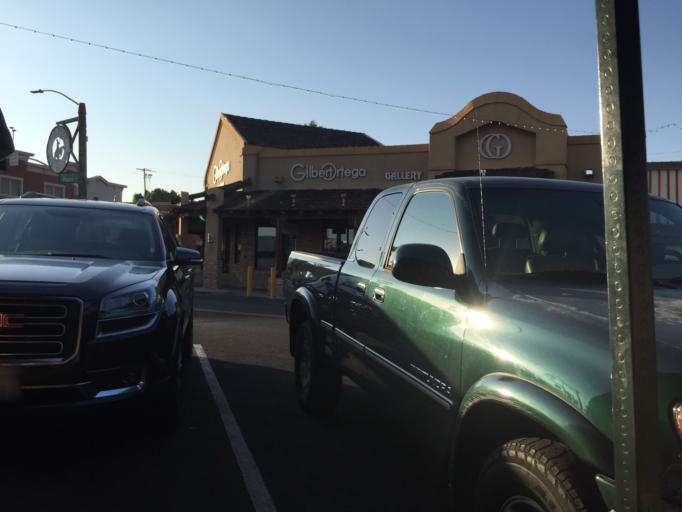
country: US
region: Arizona
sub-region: Maricopa County
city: Scottsdale
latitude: 33.4932
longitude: -111.9257
